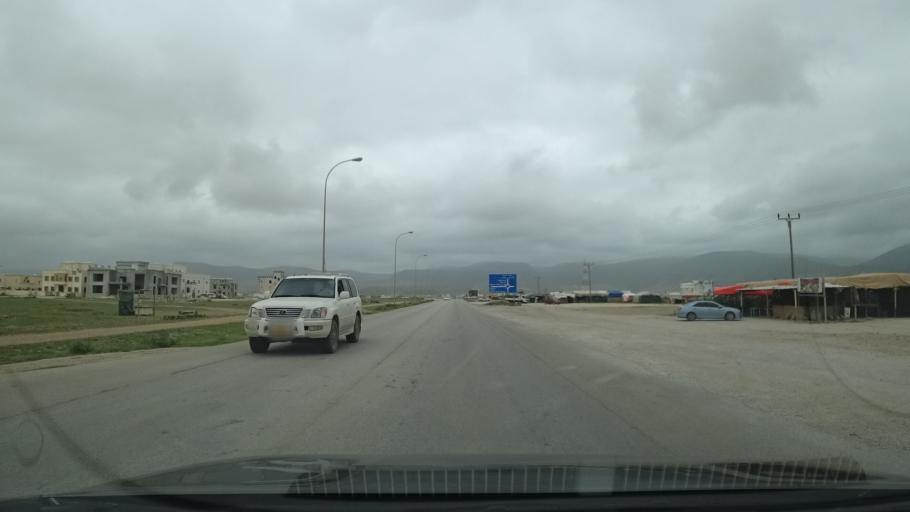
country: OM
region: Zufar
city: Salalah
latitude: 17.0988
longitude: 54.2168
